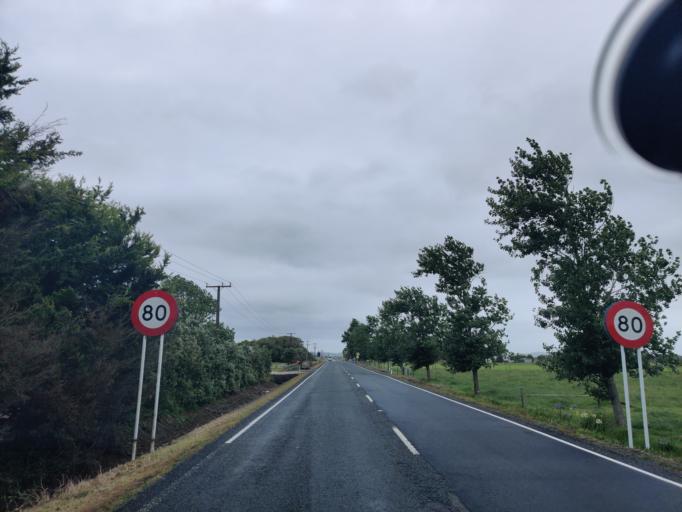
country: NZ
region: Northland
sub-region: Kaipara District
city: Dargaville
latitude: -36.1219
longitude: 174.0077
